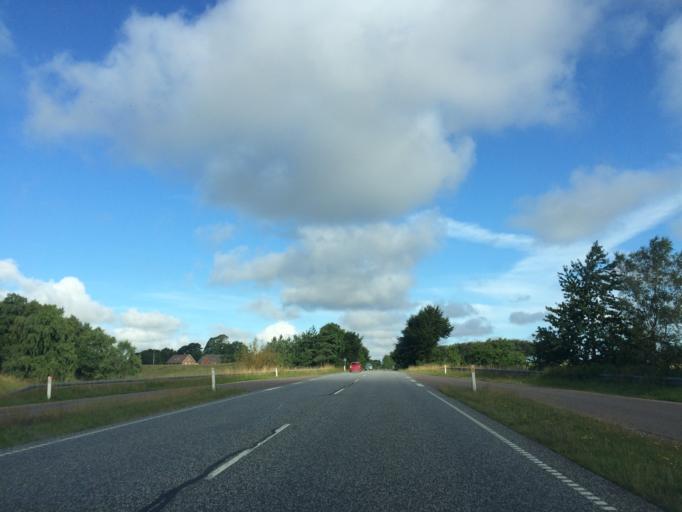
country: DK
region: Central Jutland
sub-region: Viborg Kommune
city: Bjerringbro
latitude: 56.3242
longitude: 9.5615
